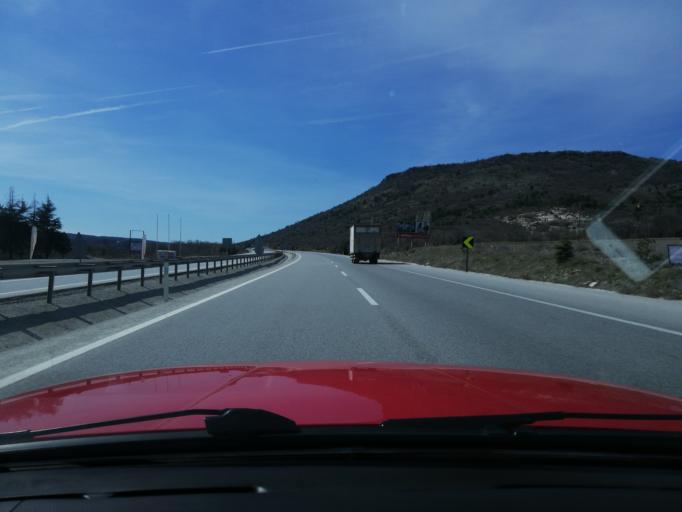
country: TR
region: Kuetahya
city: Sabuncu
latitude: 39.6052
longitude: 30.1478
